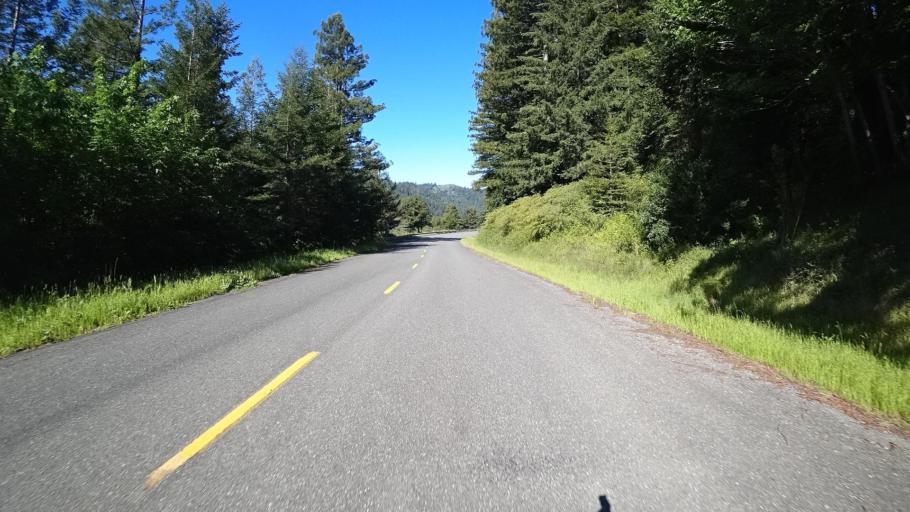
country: US
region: California
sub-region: Humboldt County
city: Rio Dell
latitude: 40.4587
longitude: -124.0666
